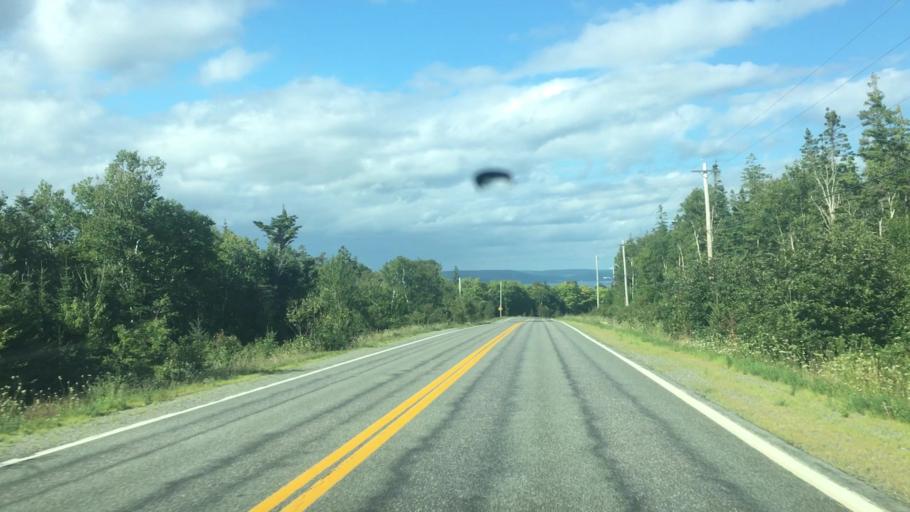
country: CA
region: Nova Scotia
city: Sydney
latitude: 45.8620
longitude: -60.6260
